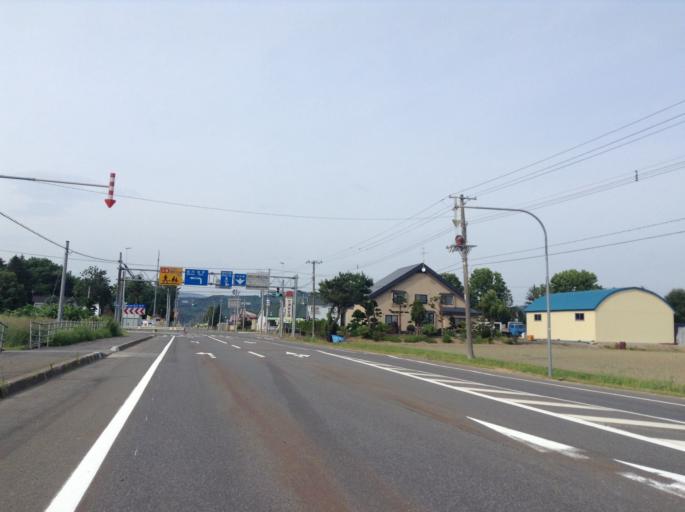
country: JP
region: Hokkaido
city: Nayoro
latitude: 44.4359
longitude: 142.4030
